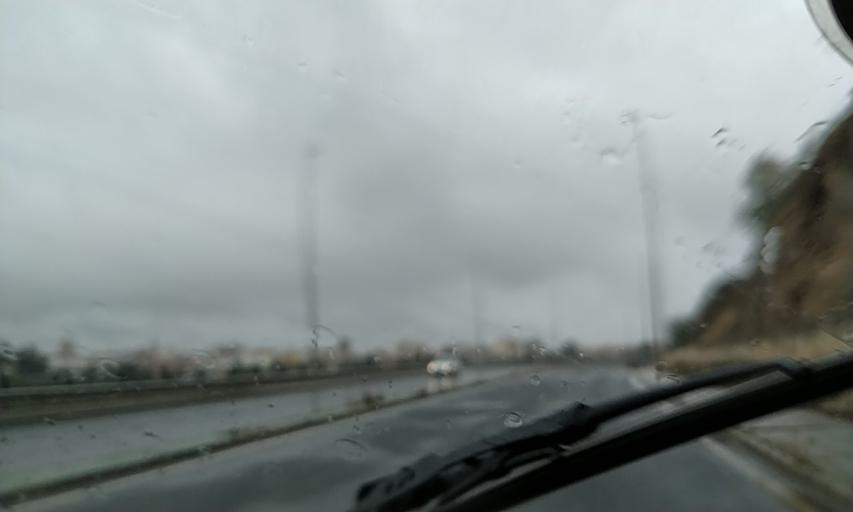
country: ES
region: Extremadura
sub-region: Provincia de Badajoz
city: Badajoz
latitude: 38.8875
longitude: -6.9722
